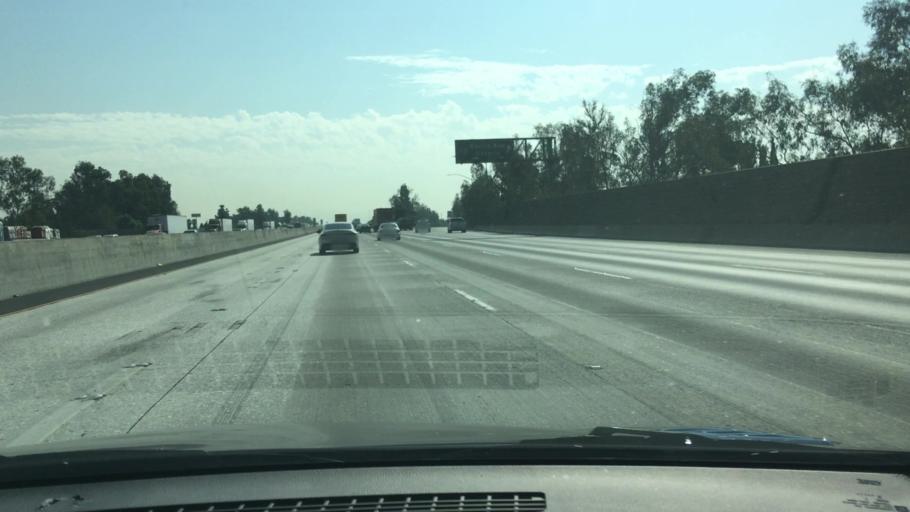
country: US
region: California
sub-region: San Bernardino County
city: Ontario
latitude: 34.0304
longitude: -117.6568
